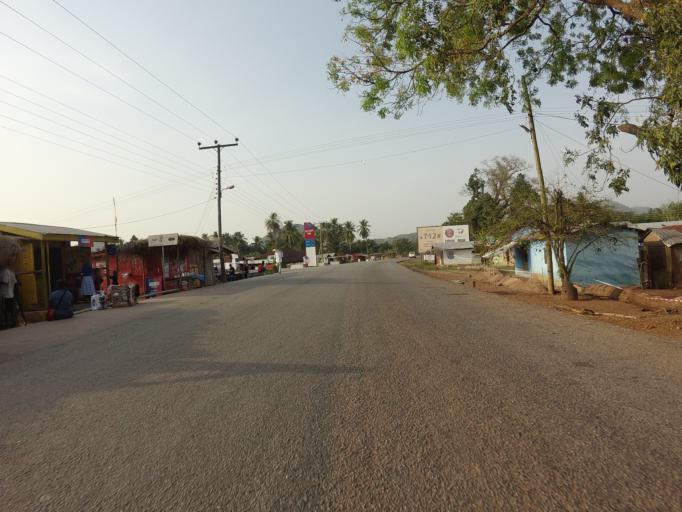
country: GH
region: Volta
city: Ho
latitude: 6.4083
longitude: 0.1727
